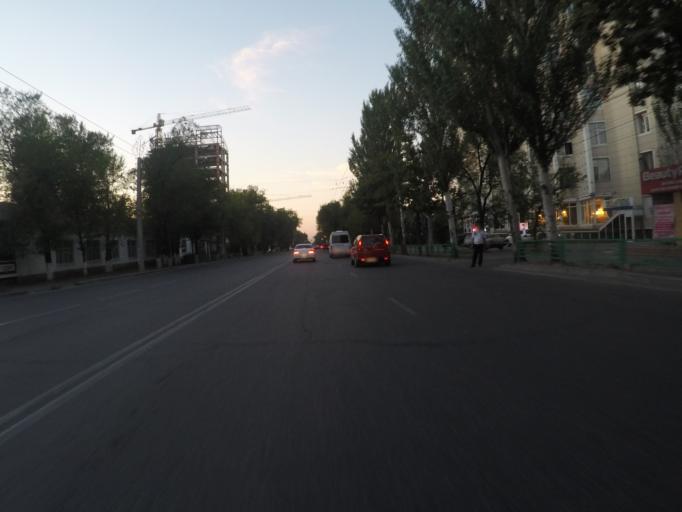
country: KG
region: Chuy
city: Bishkek
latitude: 42.8503
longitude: 74.6096
